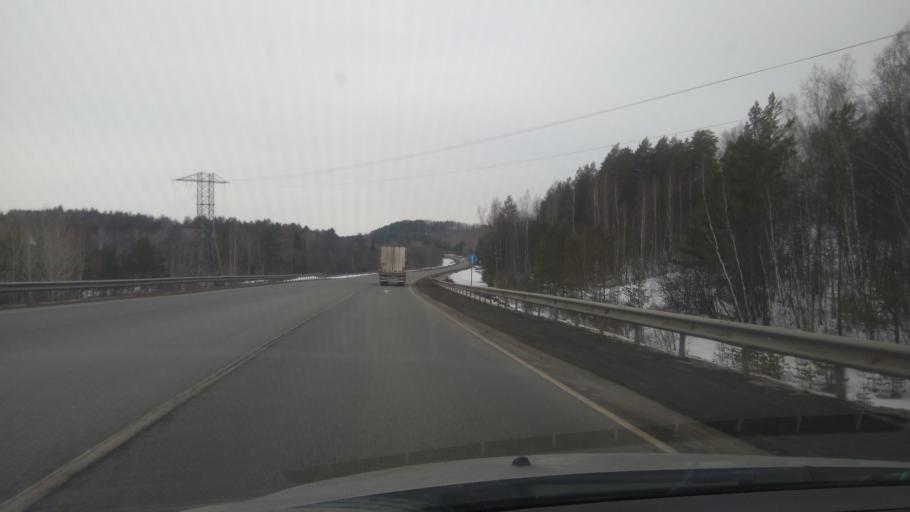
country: RU
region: Sverdlovsk
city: Ufimskiy
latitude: 56.7751
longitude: 58.2424
